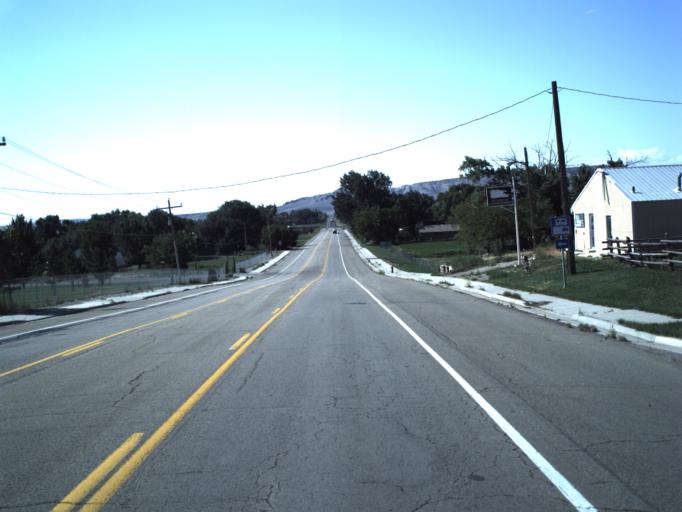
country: US
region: Utah
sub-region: Emery County
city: Ferron
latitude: 39.0875
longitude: -111.1321
